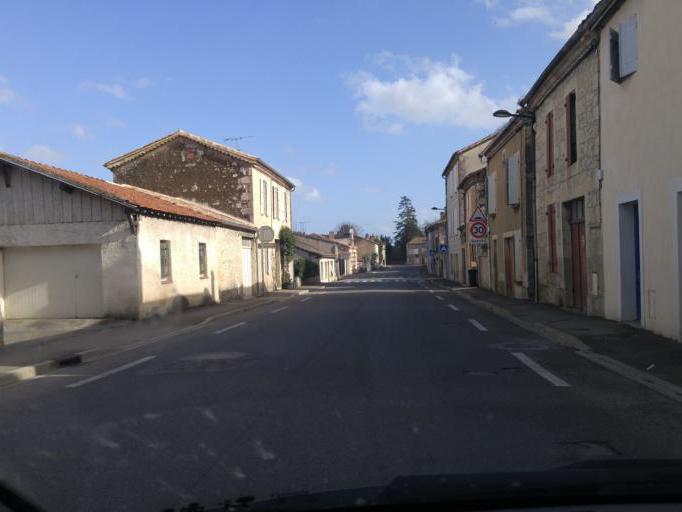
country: FR
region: Midi-Pyrenees
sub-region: Departement du Gers
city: Lectoure
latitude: 43.9340
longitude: 0.6307
